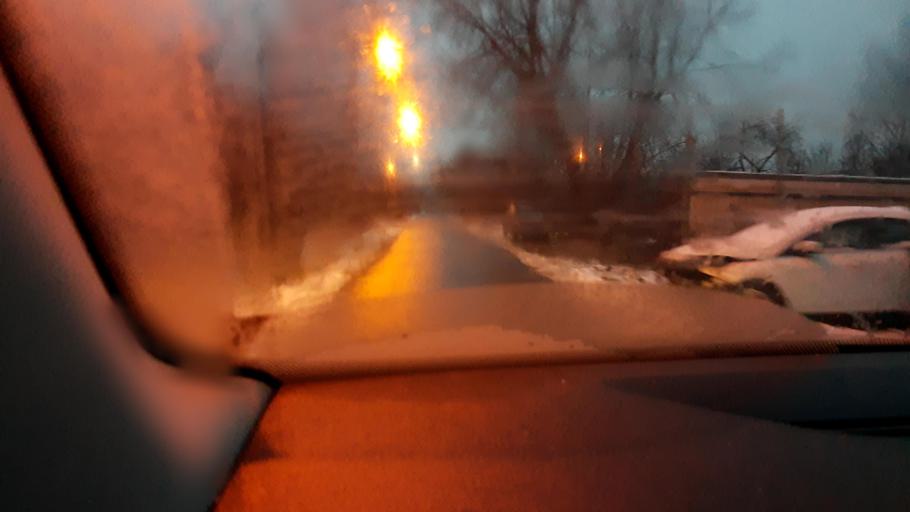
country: RU
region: Moscow
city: Annino
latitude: 55.5688
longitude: 37.6133
